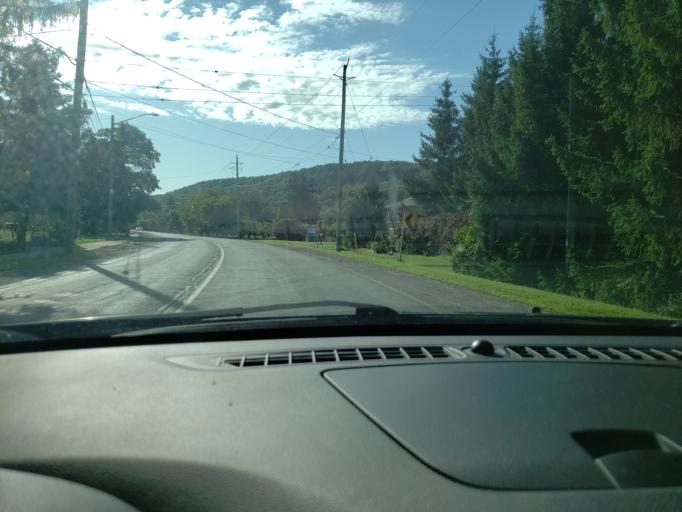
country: CA
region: Ontario
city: Hamilton
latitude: 43.1959
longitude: -79.6039
